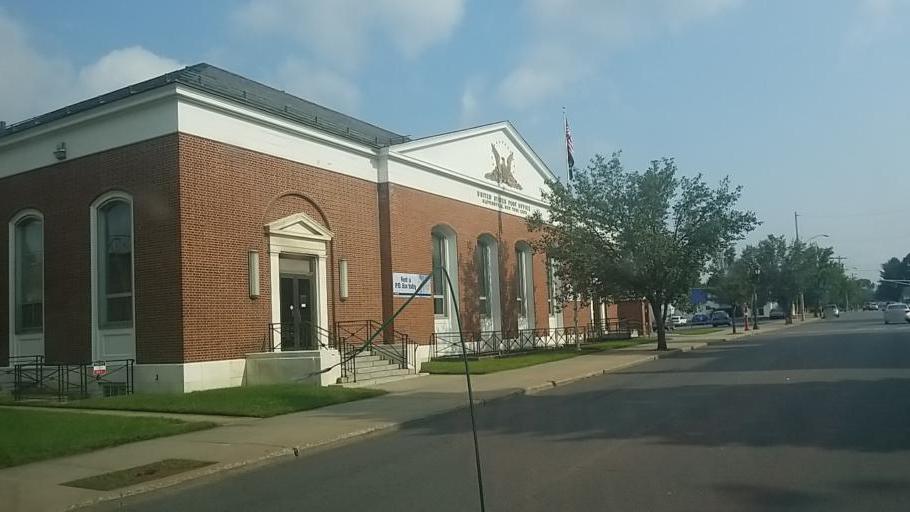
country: US
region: New York
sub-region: Fulton County
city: Gloversville
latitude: 43.0533
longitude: -74.3435
